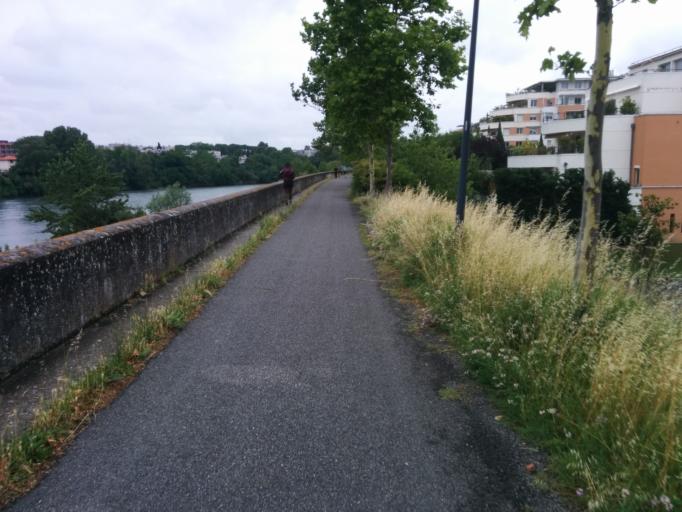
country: FR
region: Midi-Pyrenees
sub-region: Departement de la Haute-Garonne
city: Blagnac
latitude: 43.6145
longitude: 1.4064
